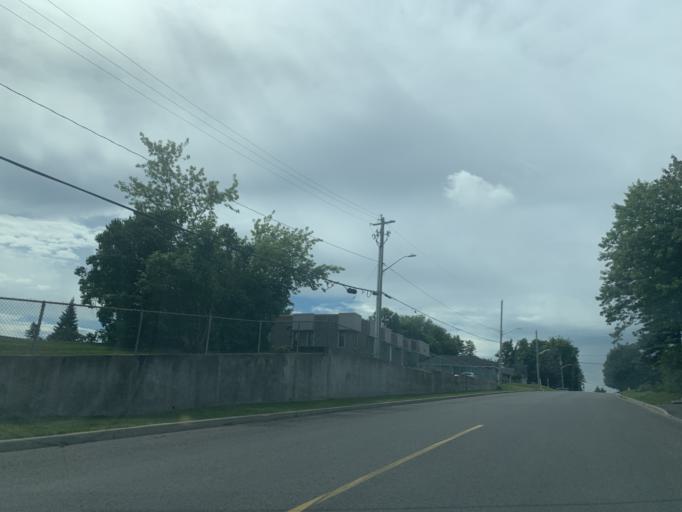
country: CA
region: Ontario
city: Hawkesbury
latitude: 45.6069
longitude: -74.6131
